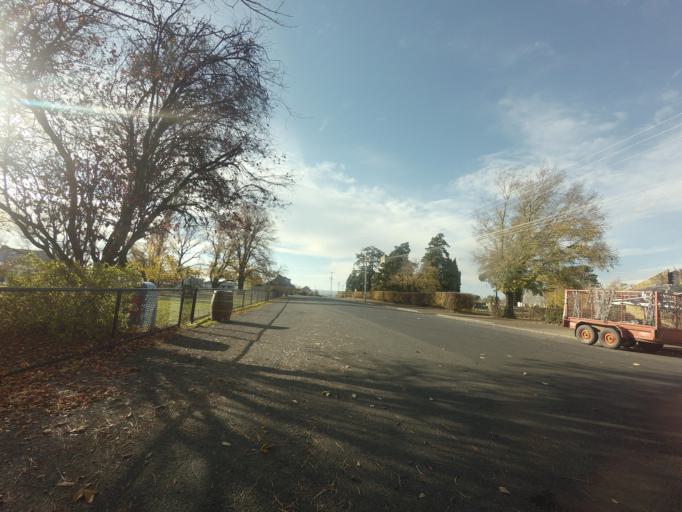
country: AU
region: Tasmania
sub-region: Derwent Valley
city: New Norfolk
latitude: -42.3830
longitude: 147.0079
